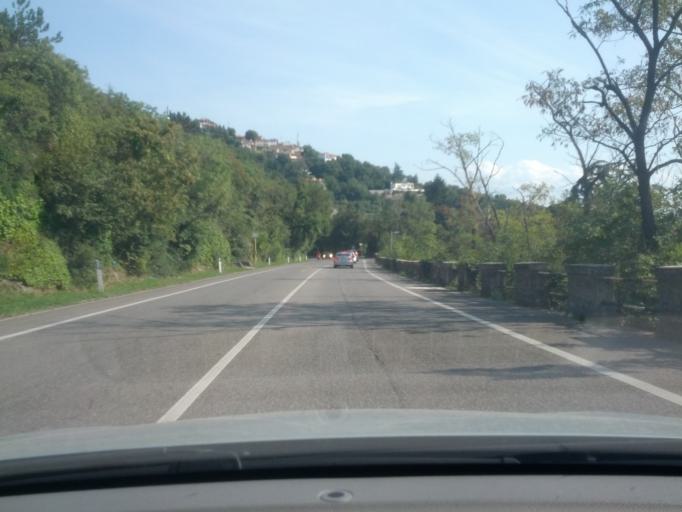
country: IT
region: Friuli Venezia Giulia
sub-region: Provincia di Trieste
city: Villa Opicina
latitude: 45.6757
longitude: 13.7885
